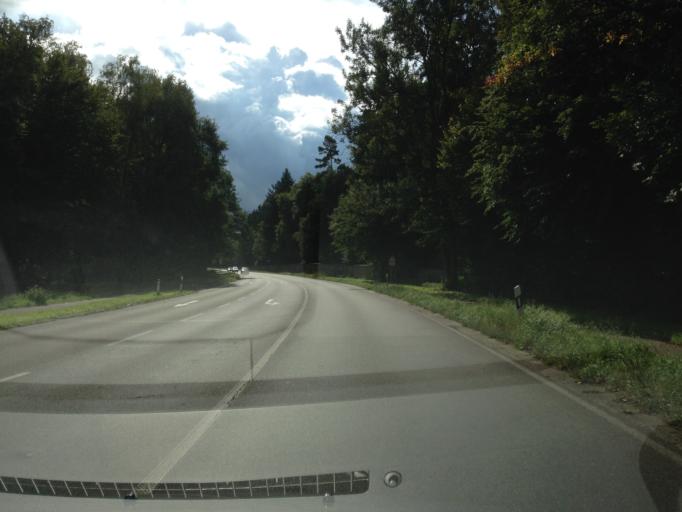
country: DE
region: North Rhine-Westphalia
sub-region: Regierungsbezirk Koln
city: Rath
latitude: 50.9093
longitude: 7.0996
